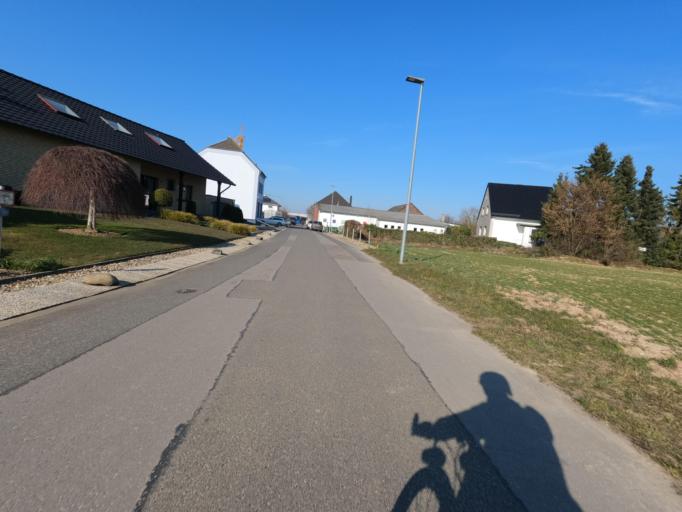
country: DE
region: North Rhine-Westphalia
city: Erkelenz
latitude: 51.0627
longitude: 6.3022
